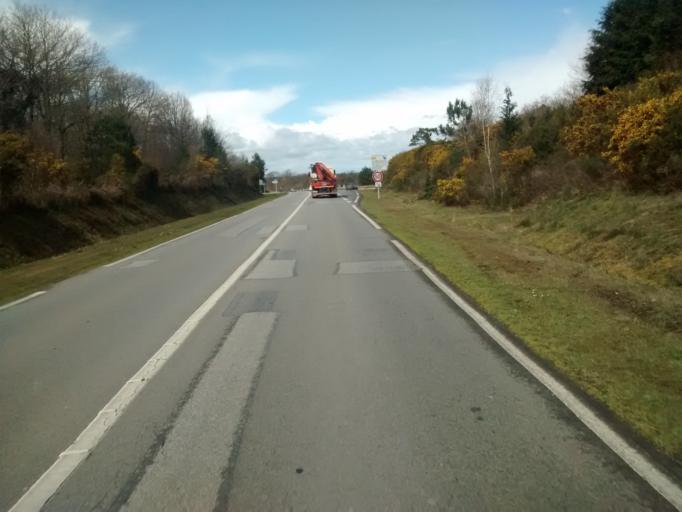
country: FR
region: Brittany
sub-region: Departement du Morbihan
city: Molac
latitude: 47.7522
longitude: -2.4385
